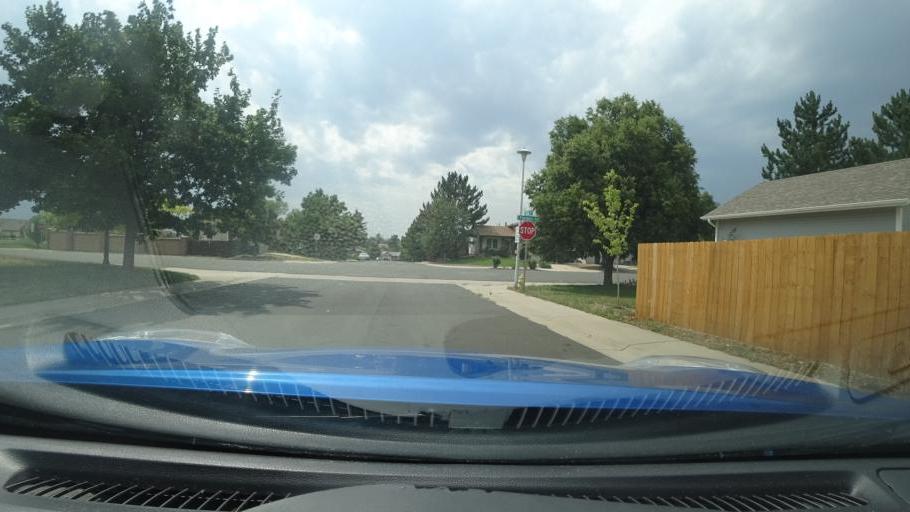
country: US
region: Colorado
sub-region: Adams County
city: Aurora
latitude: 39.6826
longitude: -104.7599
